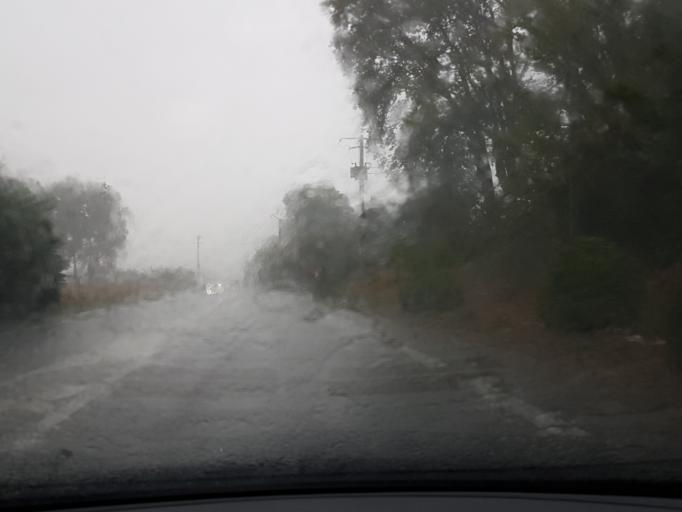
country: FR
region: Provence-Alpes-Cote d'Azur
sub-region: Departement du Vaucluse
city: Velleron
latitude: 43.9821
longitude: 5.0166
